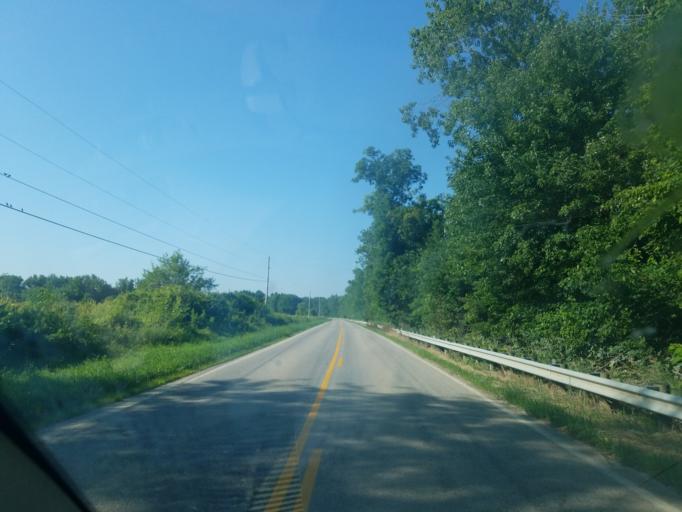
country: US
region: Ohio
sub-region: Marion County
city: Prospect
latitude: 40.4694
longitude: -83.1907
